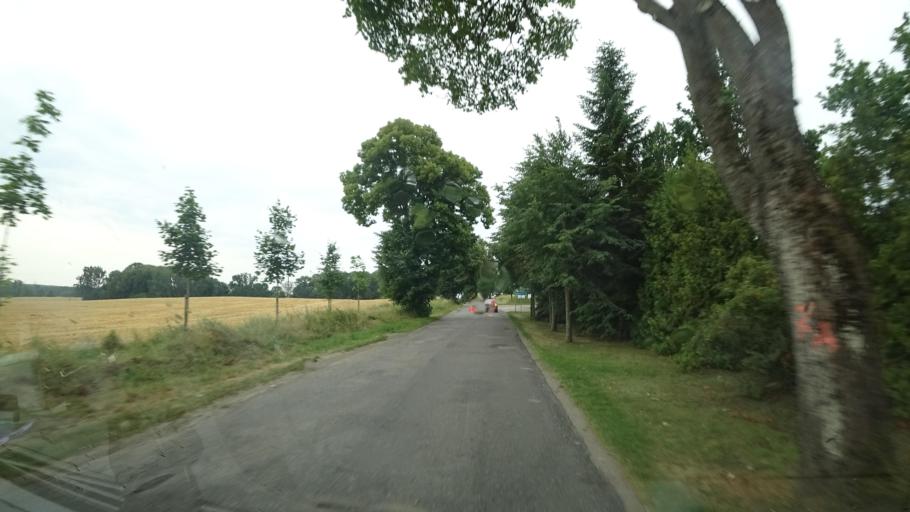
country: PL
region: Warmian-Masurian Voivodeship
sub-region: Powiat gizycki
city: Ryn
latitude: 53.9288
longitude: 21.5505
